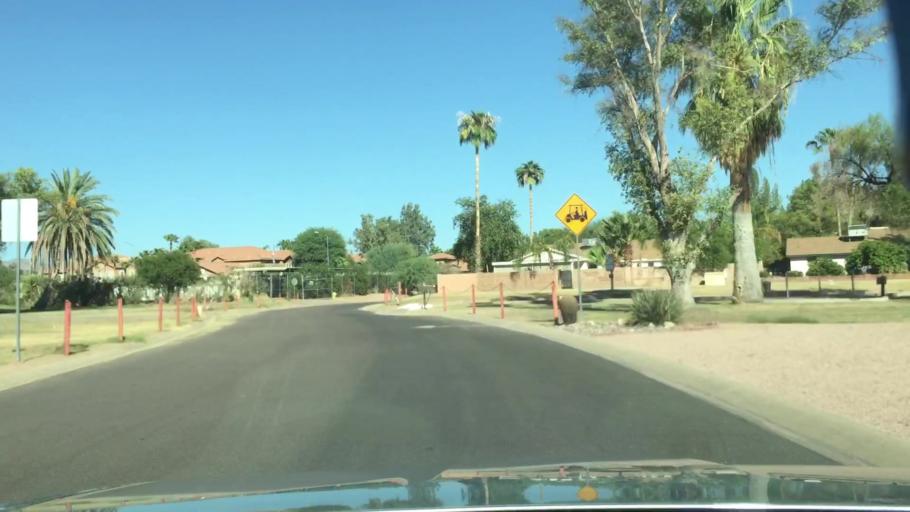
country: US
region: Arizona
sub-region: Maricopa County
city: Gilbert
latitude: 33.4062
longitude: -111.6774
